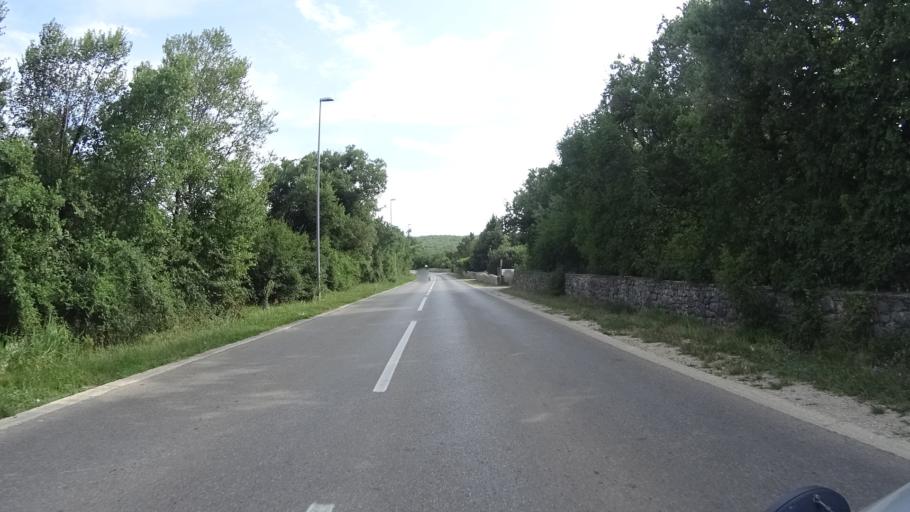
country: HR
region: Istarska
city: Rasa
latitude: 45.0781
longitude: 14.0962
